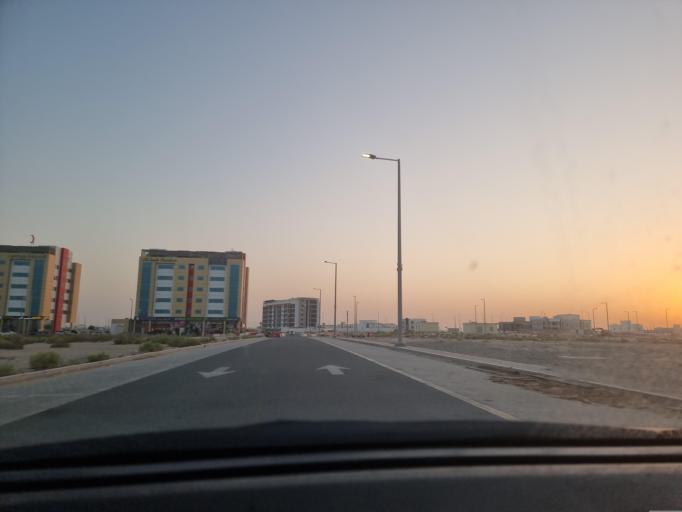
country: AE
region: Abu Dhabi
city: Abu Dhabi
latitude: 24.3698
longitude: 54.7406
